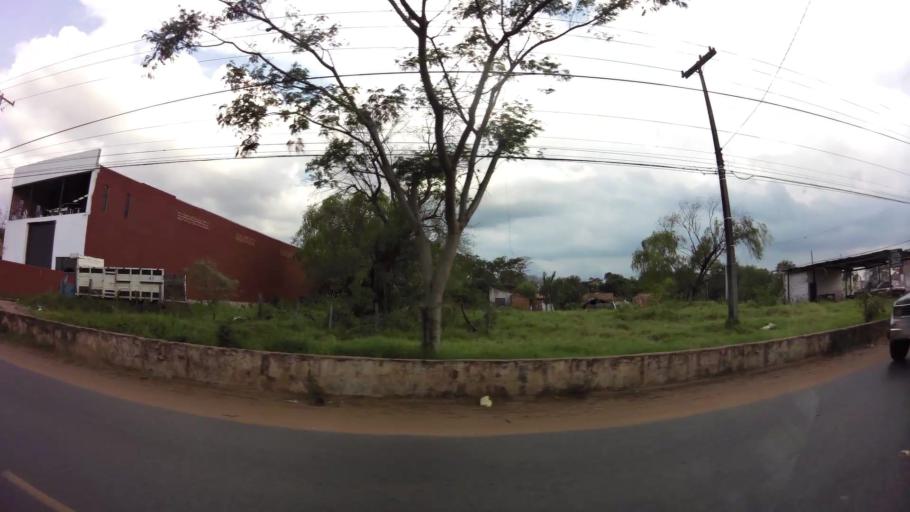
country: PY
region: Central
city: Villa Elisa
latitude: -25.3566
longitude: -57.5598
